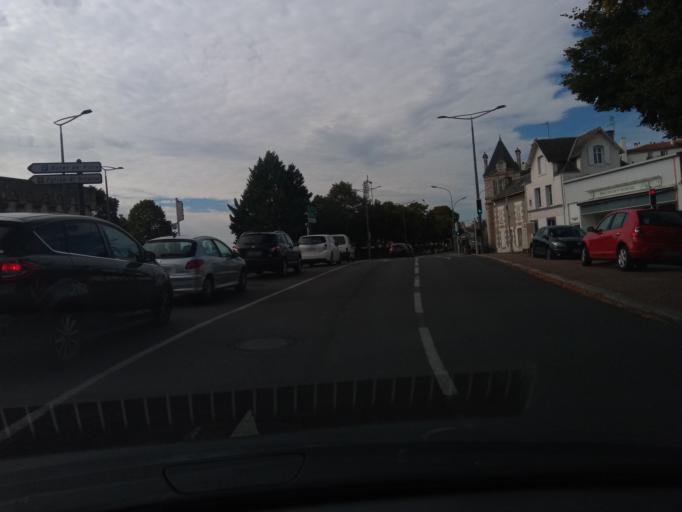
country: FR
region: Poitou-Charentes
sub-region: Departement de la Vienne
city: Poitiers
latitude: 46.5742
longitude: 0.3295
